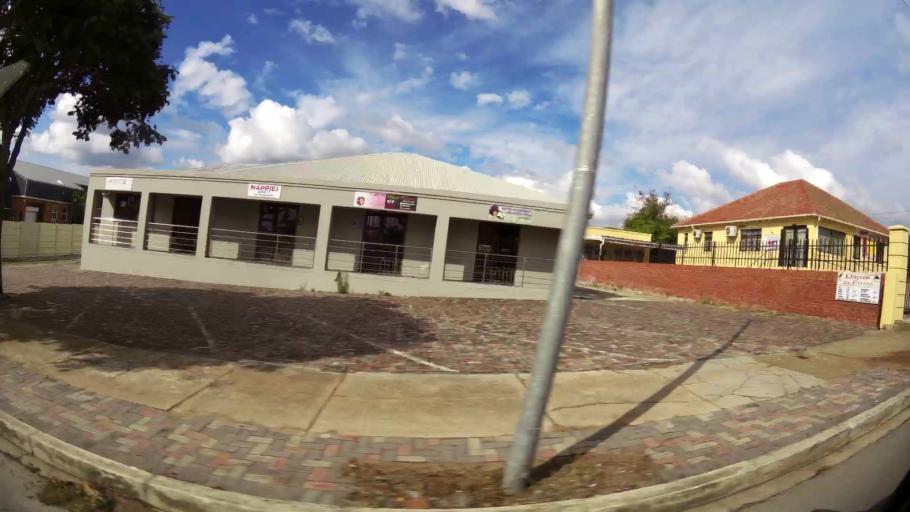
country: ZA
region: Eastern Cape
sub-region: Nelson Mandela Bay Metropolitan Municipality
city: Port Elizabeth
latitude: -33.9456
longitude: 25.5696
